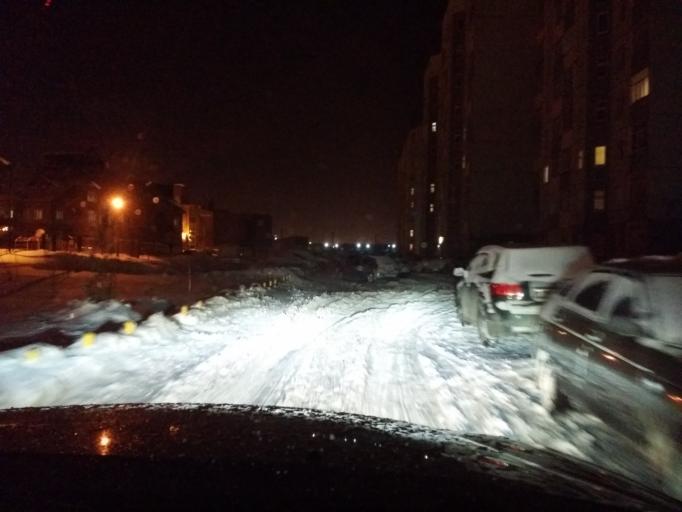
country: RU
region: Khanty-Mansiyskiy Avtonomnyy Okrug
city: Nizhnevartovsk
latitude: 60.9573
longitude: 76.5772
